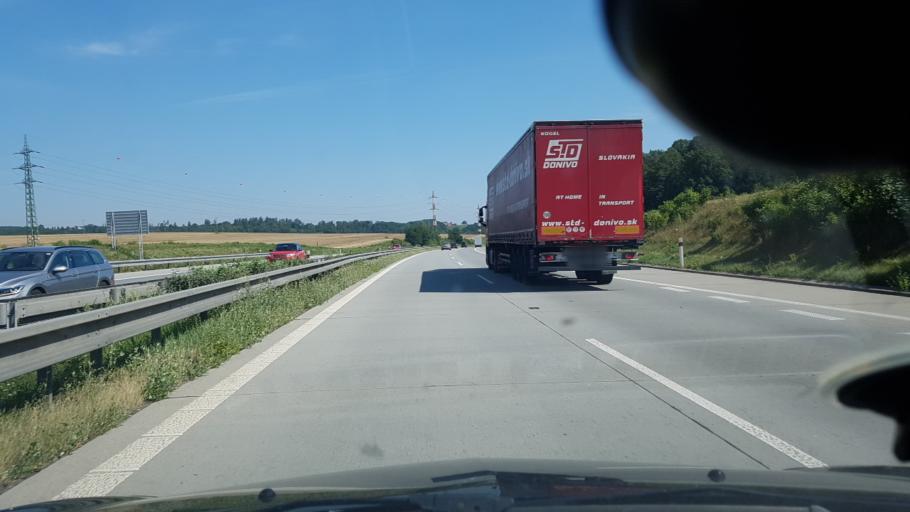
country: CZ
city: Klimkovice
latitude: 49.7808
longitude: 18.0990
